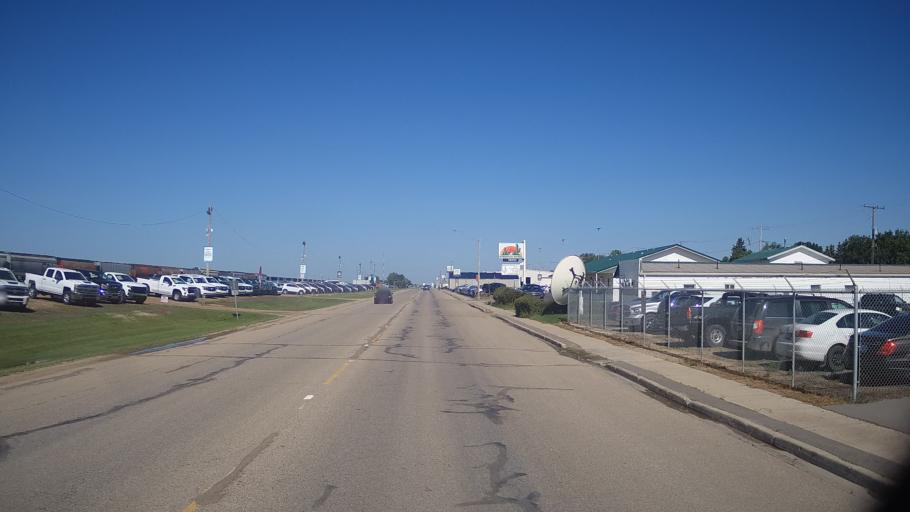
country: CA
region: Saskatchewan
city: Watrous
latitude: 51.6692
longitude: -105.4611
